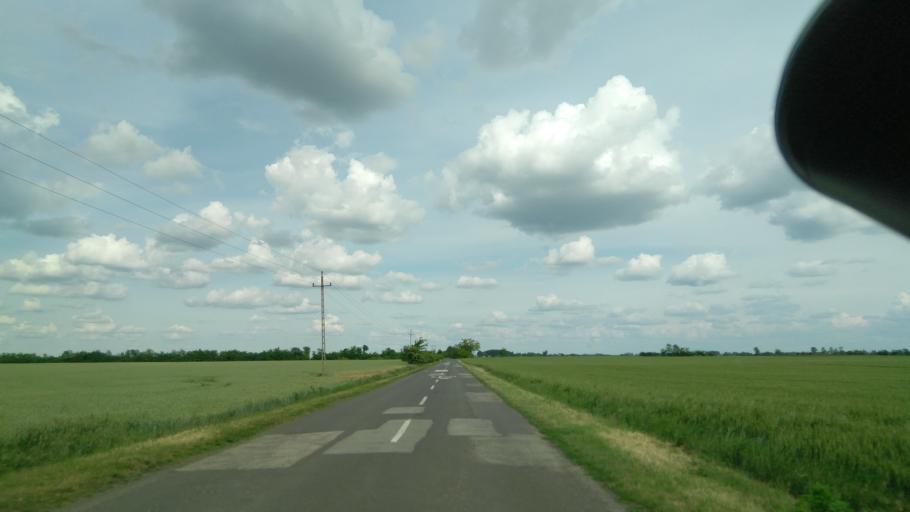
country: RO
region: Arad
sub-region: Comuna Peregu Mare
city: Peregu Mic
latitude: 46.2980
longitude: 20.9483
